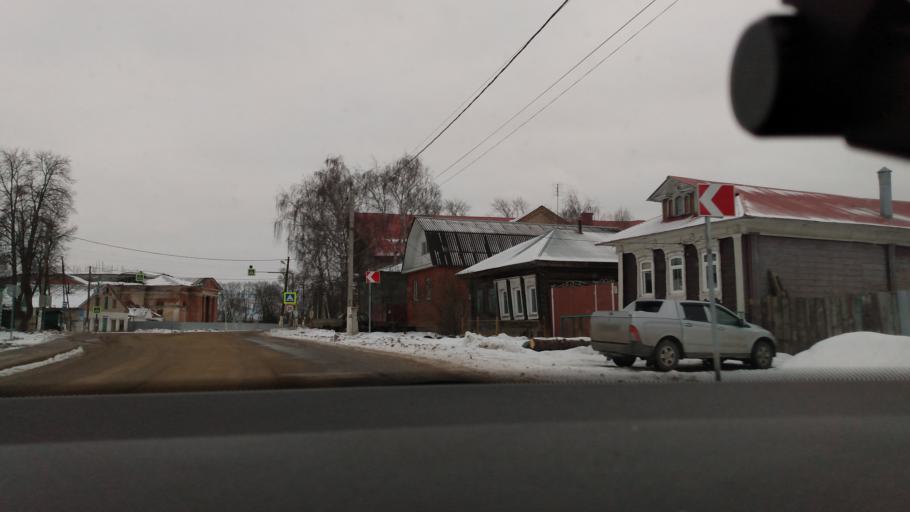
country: RU
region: Moskovskaya
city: Krasnaya Poyma
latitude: 55.0564
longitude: 39.1118
